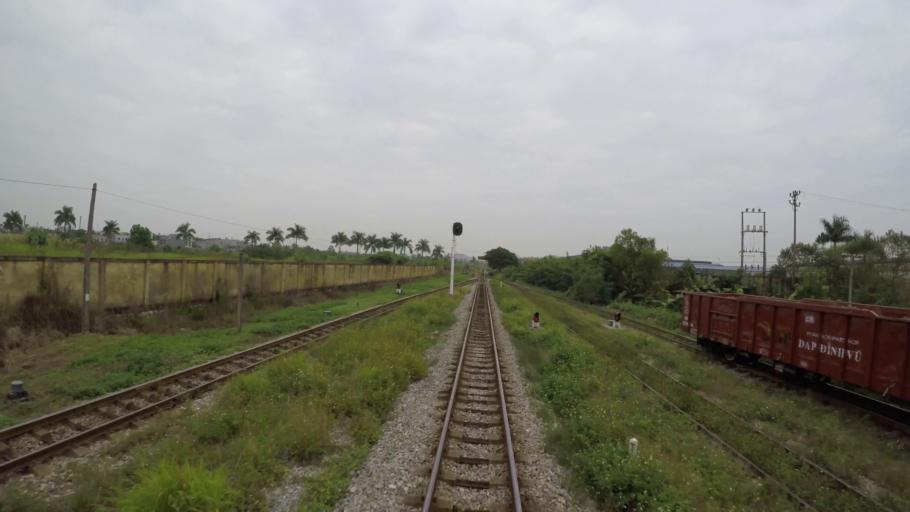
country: VN
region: Hai Phong
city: An Duong
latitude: 20.9048
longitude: 106.5753
